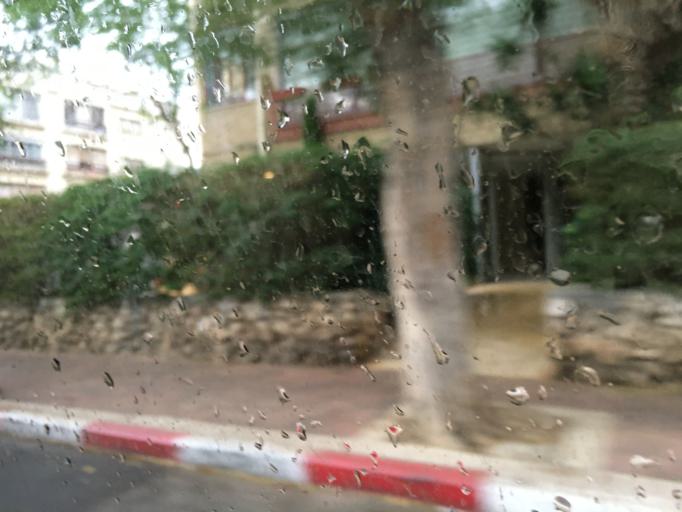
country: IL
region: Tel Aviv
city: Ramat HaSharon
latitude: 32.1401
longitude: 34.8403
